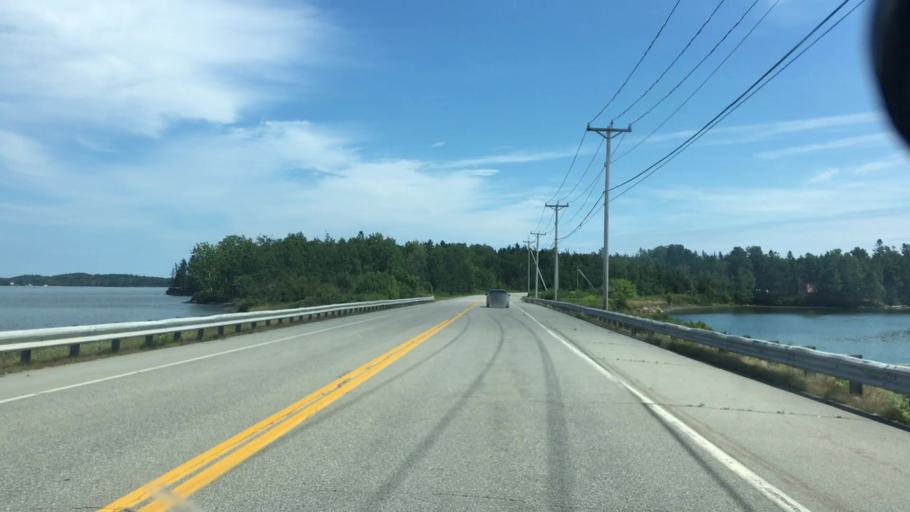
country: US
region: Maine
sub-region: Washington County
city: Eastport
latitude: 44.9388
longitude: -67.0319
